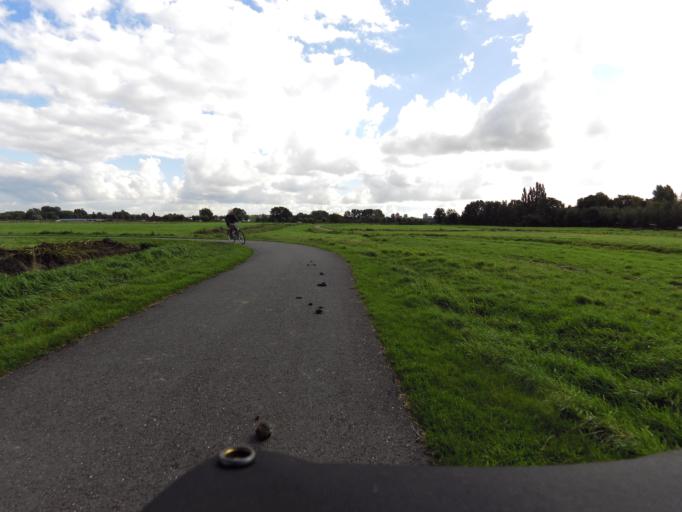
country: NL
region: South Holland
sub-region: Gemeente Vlaardingen
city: Vlaardingen
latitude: 51.9491
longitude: 4.3495
